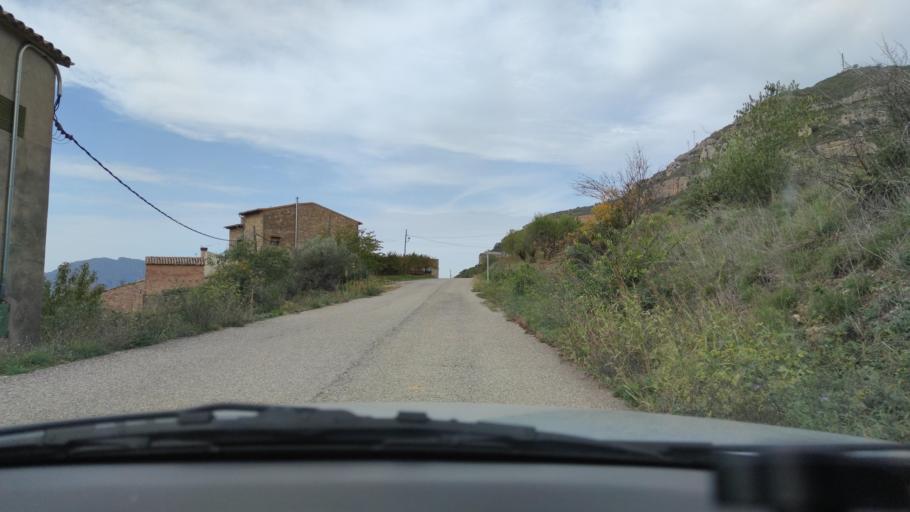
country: ES
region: Catalonia
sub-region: Provincia de Lleida
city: Llimiana
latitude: 42.0689
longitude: 0.9441
